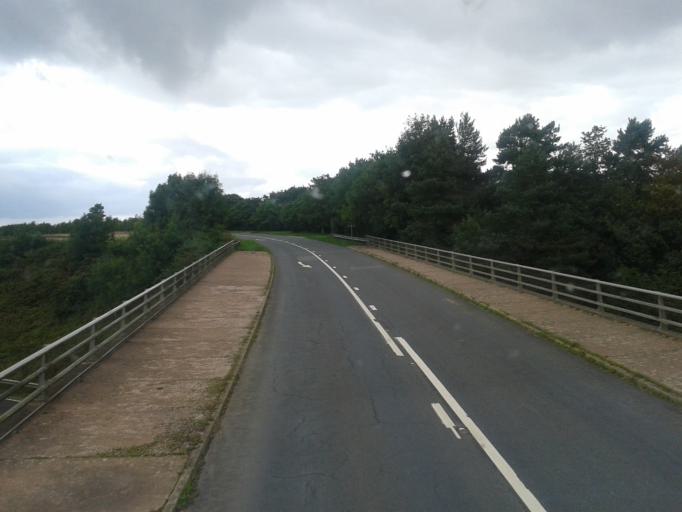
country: GB
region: England
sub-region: Devon
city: Crediton
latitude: 50.7187
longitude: -3.7935
